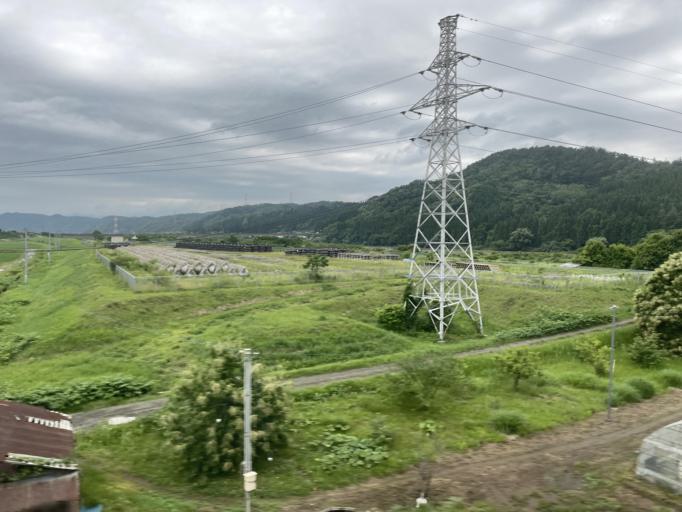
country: JP
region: Akita
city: Takanosu
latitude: 40.2033
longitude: 140.2126
